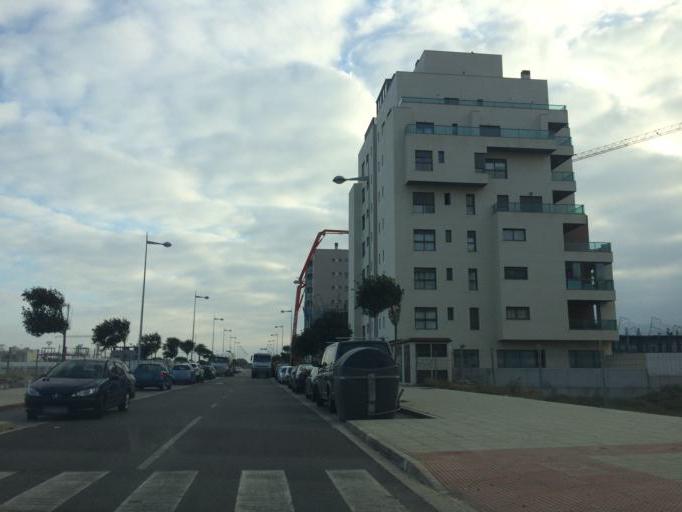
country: ES
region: Andalusia
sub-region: Provincia de Almeria
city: Almeria
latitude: 36.8282
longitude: -2.4422
